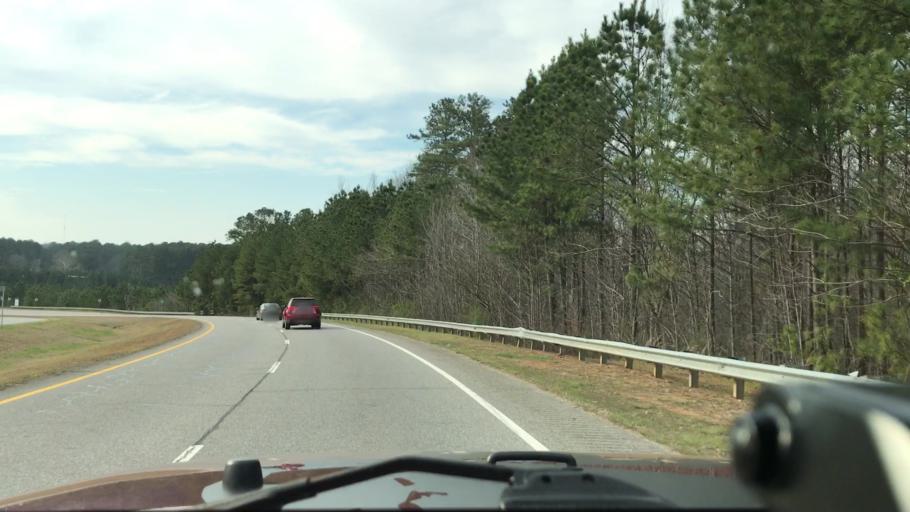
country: US
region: Georgia
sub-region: Cherokee County
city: Canton
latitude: 34.2579
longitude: -84.4825
